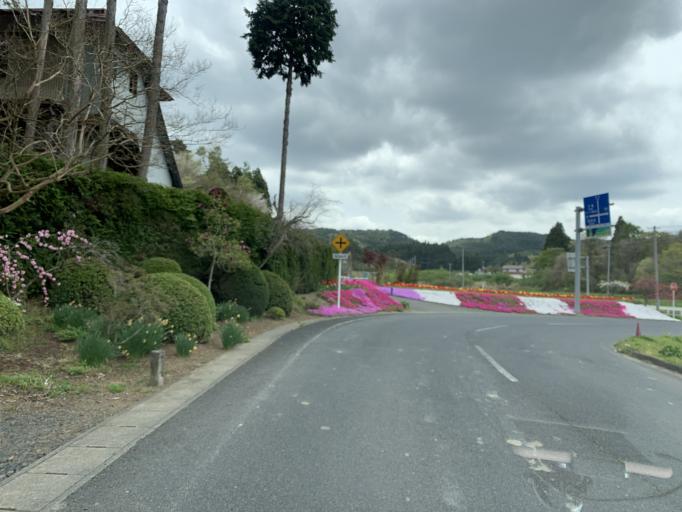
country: JP
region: Iwate
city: Ichinoseki
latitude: 38.8359
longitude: 141.3549
